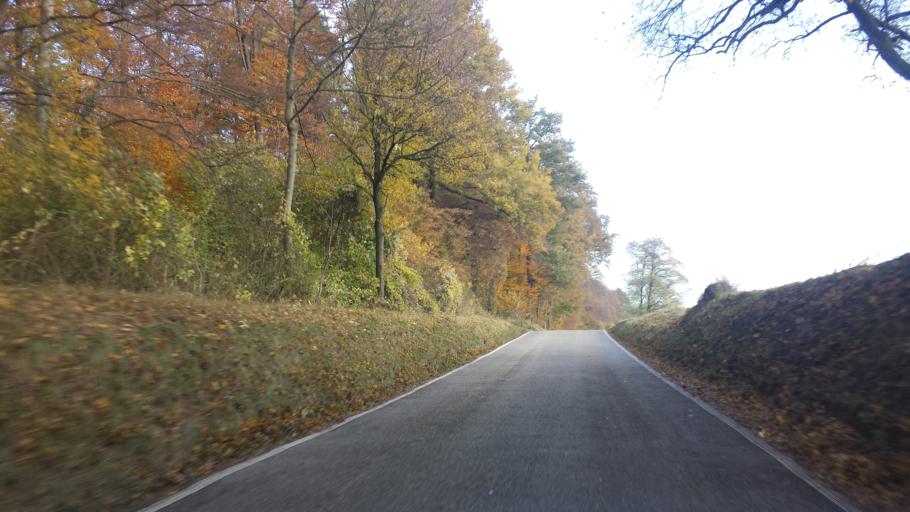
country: DE
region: Baden-Wuerttemberg
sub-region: Karlsruhe Region
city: Gondelsheim
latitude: 49.0983
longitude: 8.6991
